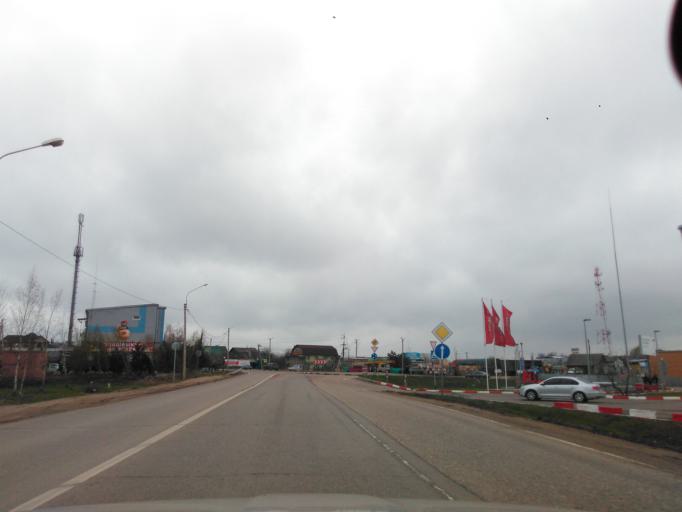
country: RU
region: Moskovskaya
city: Pavlovskaya Sloboda
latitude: 55.8158
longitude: 37.0714
